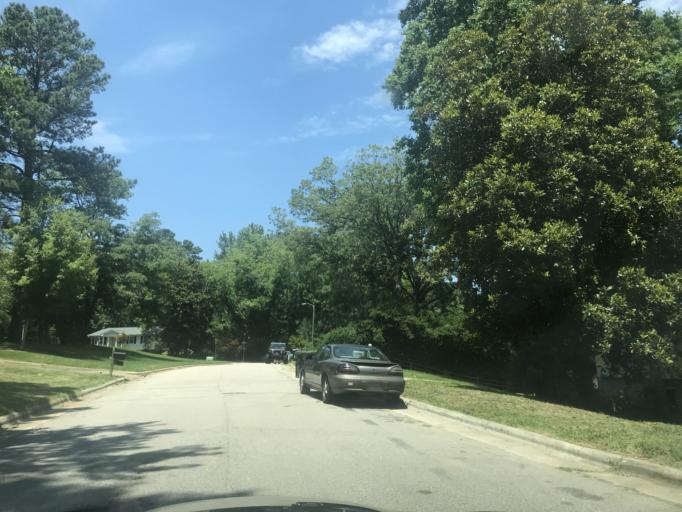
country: US
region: North Carolina
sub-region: Wake County
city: West Raleigh
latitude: 35.8904
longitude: -78.6221
